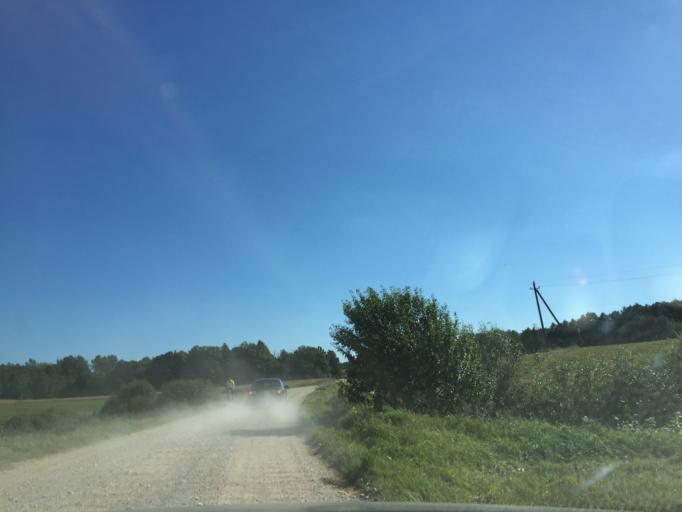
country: LT
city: Zarasai
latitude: 55.7980
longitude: 25.9506
